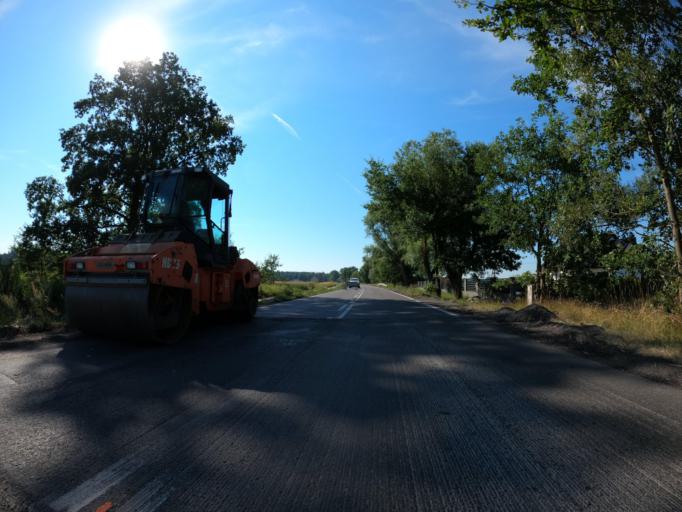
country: PL
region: West Pomeranian Voivodeship
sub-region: Powiat goleniowski
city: Goleniow
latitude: 53.6193
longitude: 14.7390
